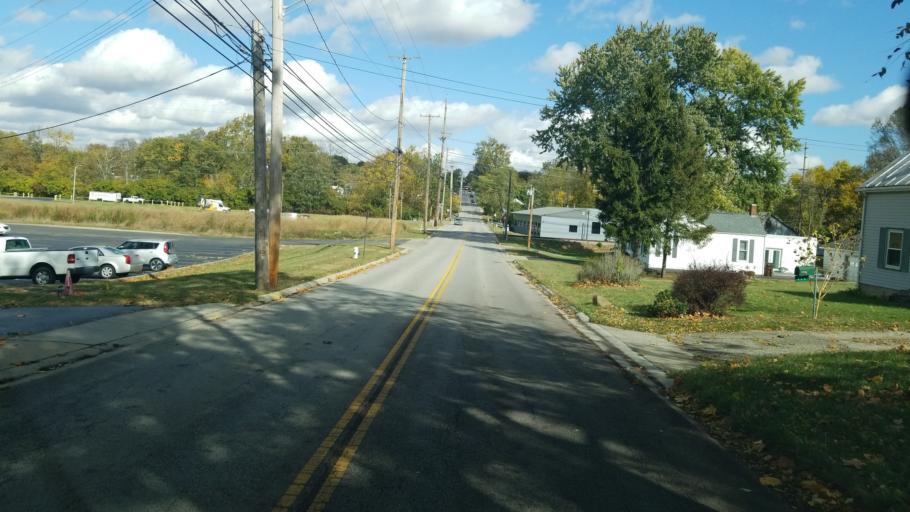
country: US
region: Ohio
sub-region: Warren County
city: Lebanon
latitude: 39.4310
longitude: -84.2158
